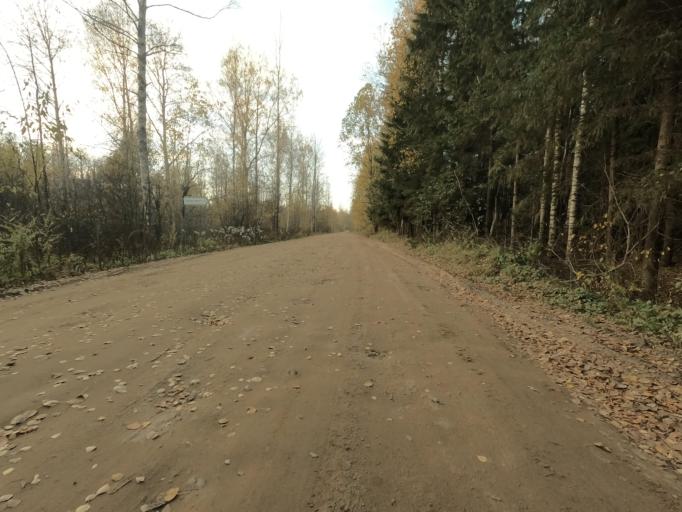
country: RU
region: Leningrad
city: Priladozhskiy
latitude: 59.7465
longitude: 31.3053
